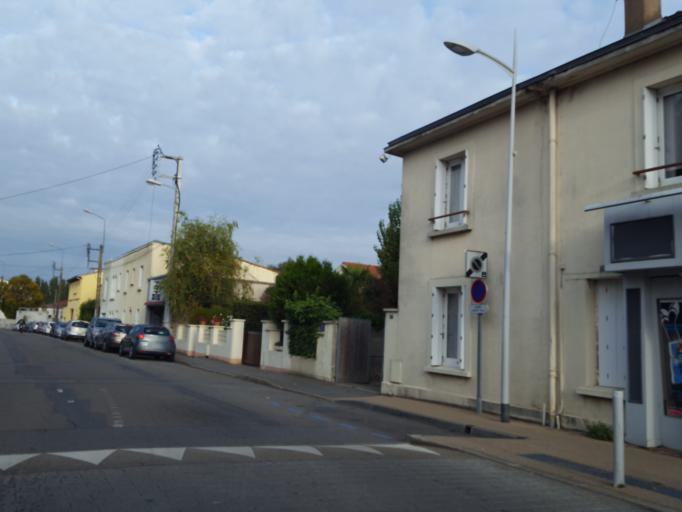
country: FR
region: Pays de la Loire
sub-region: Departement de la Loire-Atlantique
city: Saint-Sebastien-sur-Loire
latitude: 47.2087
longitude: -1.5044
